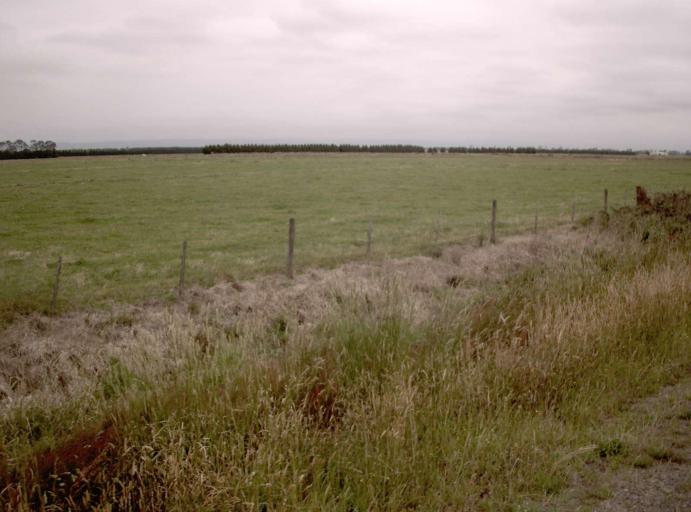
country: AU
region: Victoria
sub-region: Wellington
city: Heyfield
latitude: -38.0918
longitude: 146.7725
